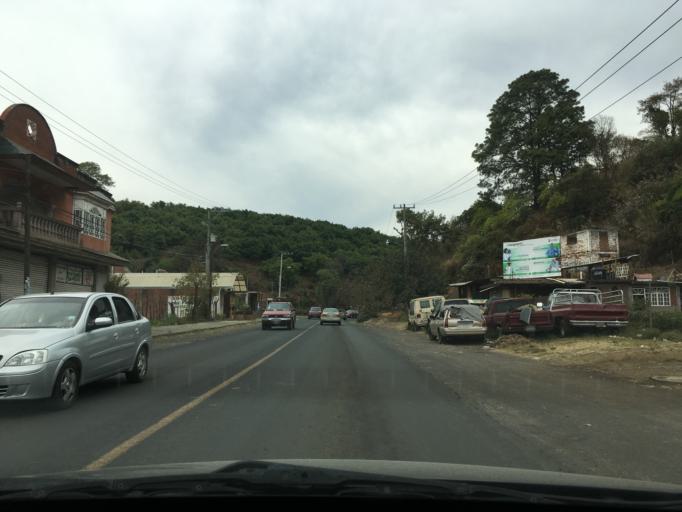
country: MX
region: Michoacan
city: Nuevo San Juan Parangaricutiro
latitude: 19.4134
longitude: -102.1215
